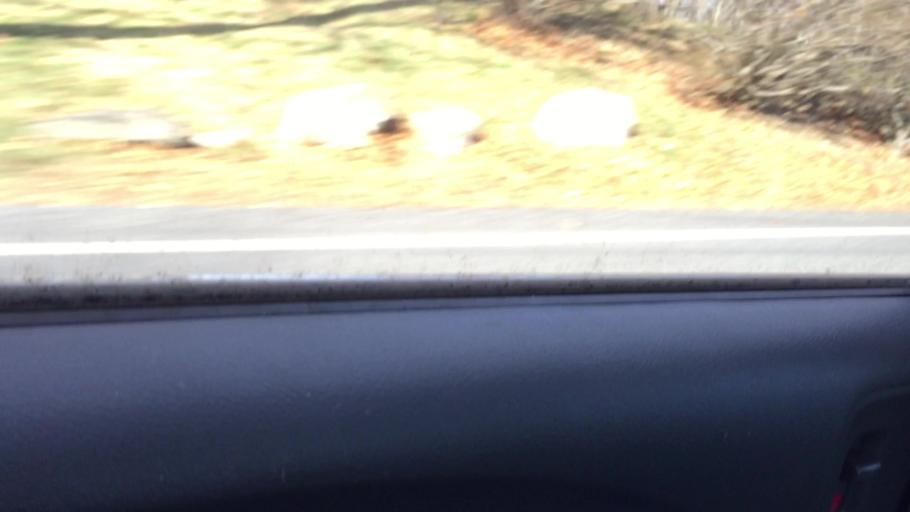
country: US
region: Massachusetts
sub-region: Barnstable County
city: Falmouth
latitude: 41.5327
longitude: -70.6602
